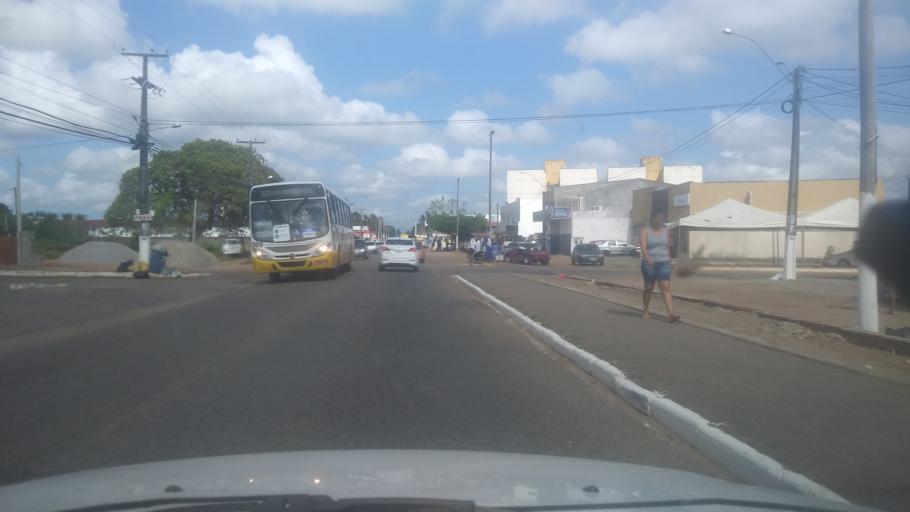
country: BR
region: Rio Grande do Norte
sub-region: Extremoz
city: Extremoz
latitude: -5.7045
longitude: -35.2933
